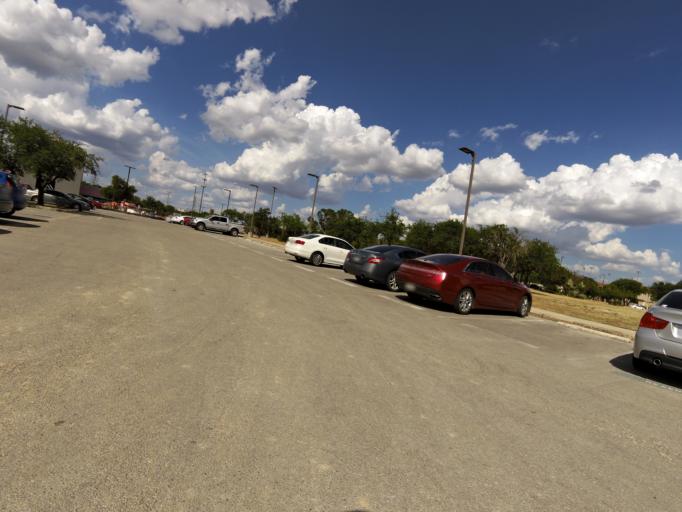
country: US
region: Texas
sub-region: Bexar County
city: Helotes
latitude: 29.5847
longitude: -98.6295
